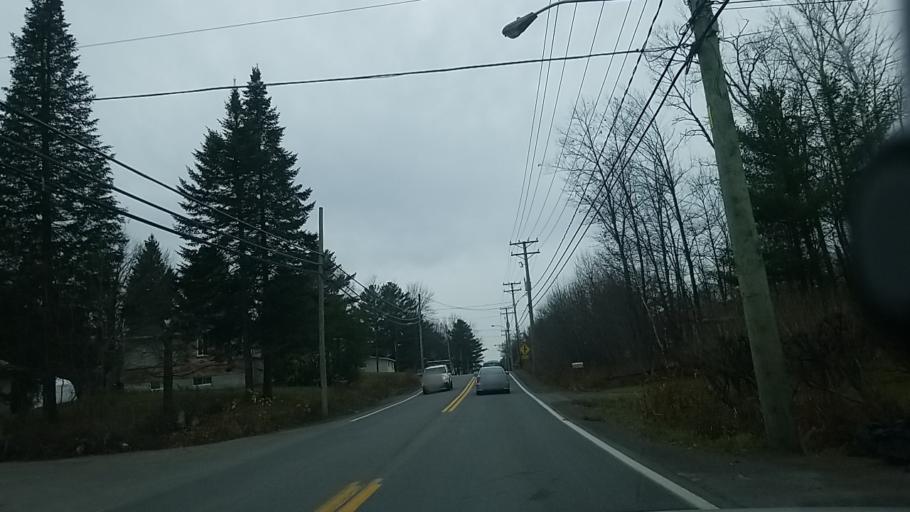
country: CA
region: Quebec
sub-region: Laurentides
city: Saint-Jerome
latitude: 45.7896
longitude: -74.0583
